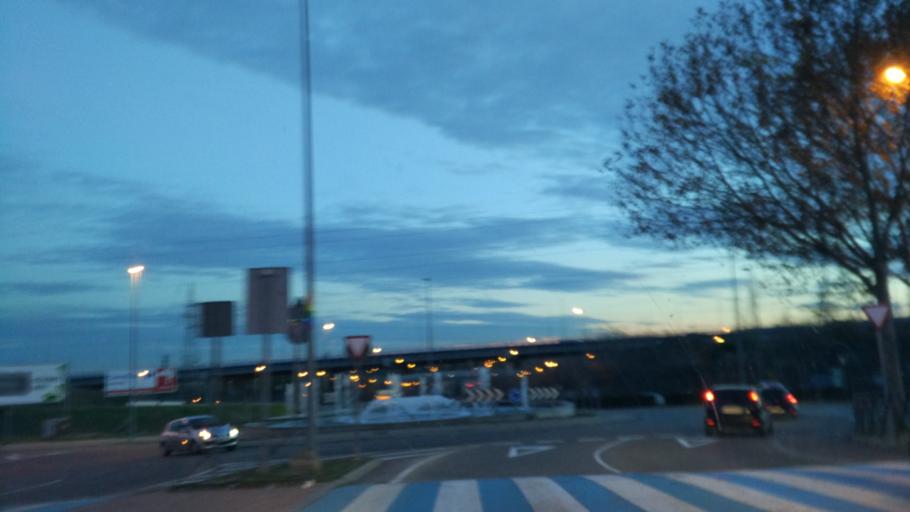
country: ES
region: Madrid
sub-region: Provincia de Madrid
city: Leganes
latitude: 40.3559
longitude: -3.7737
